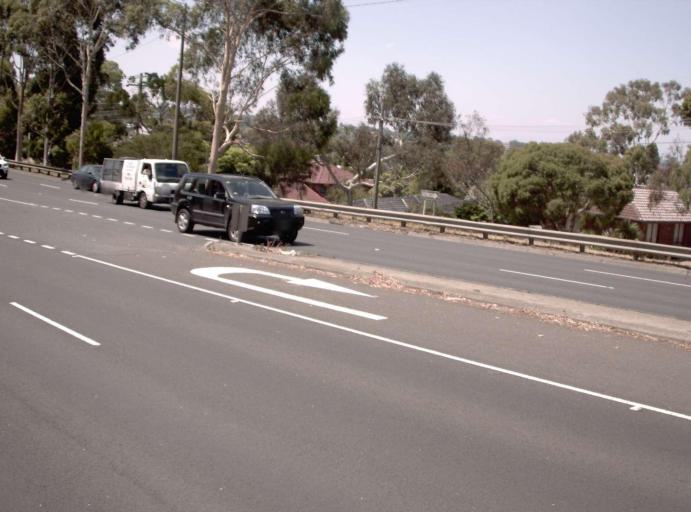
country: AU
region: Victoria
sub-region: Whitehorse
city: Vermont South
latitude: -37.8666
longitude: 145.1683
